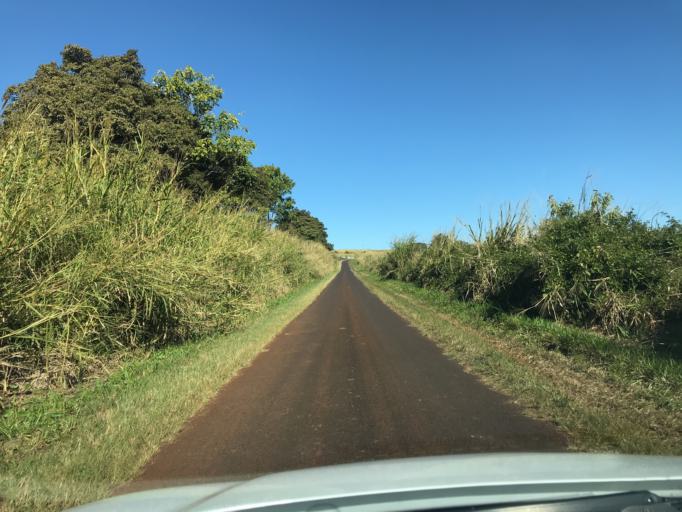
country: AU
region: Queensland
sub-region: Tablelands
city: Atherton
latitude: -17.2888
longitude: 145.5436
